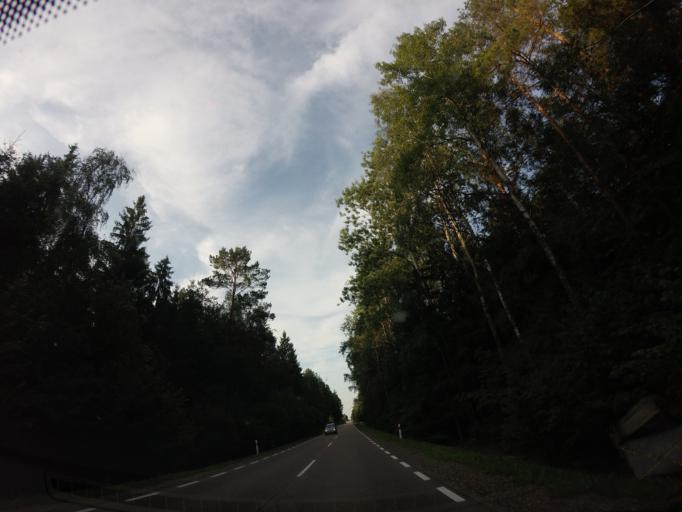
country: PL
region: Podlasie
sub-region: Powiat sejnenski
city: Sejny
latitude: 54.0196
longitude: 23.3388
